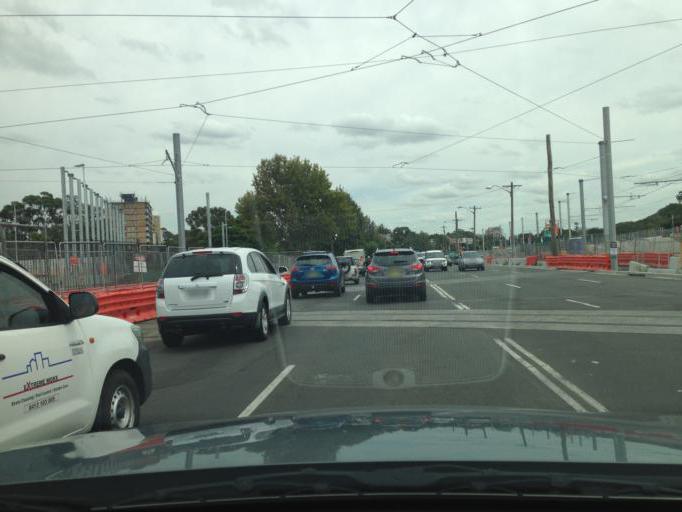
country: AU
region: New South Wales
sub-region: Randwick
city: Kensington
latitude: -33.9051
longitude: 151.2280
